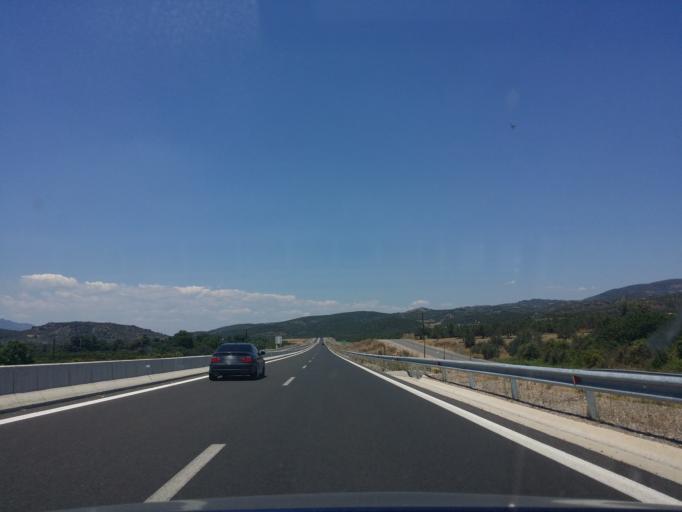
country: GR
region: Peloponnese
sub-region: Nomos Lakonias
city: Sparti
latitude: 37.1023
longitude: 22.4254
